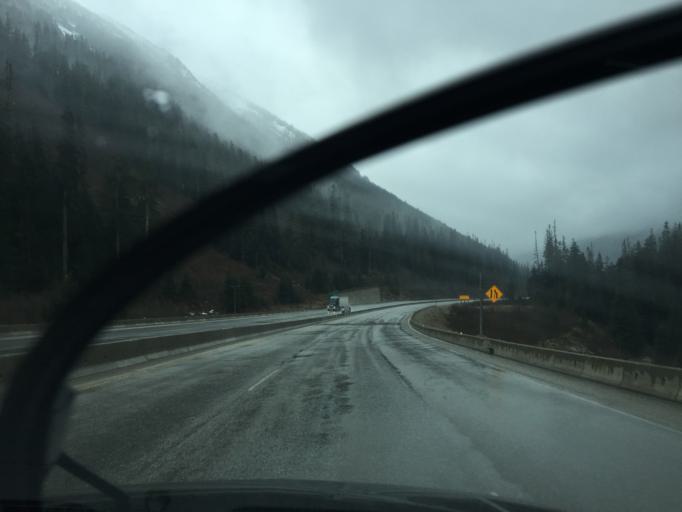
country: CA
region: British Columbia
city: Hope
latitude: 49.5906
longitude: -121.1640
